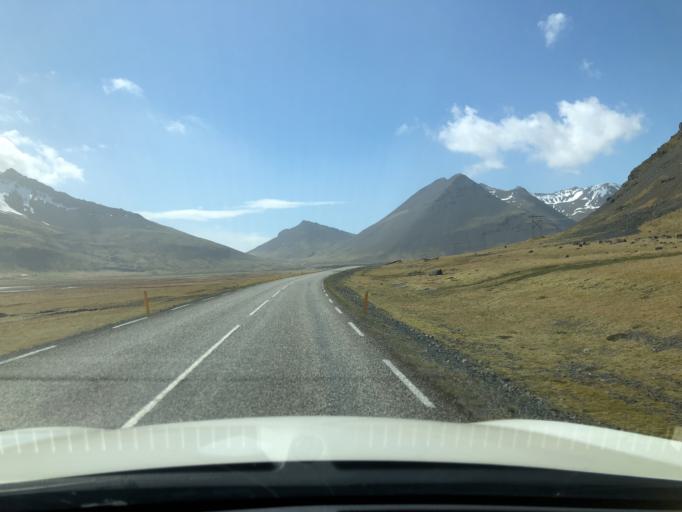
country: IS
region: East
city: Hoefn
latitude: 64.3186
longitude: -14.9530
